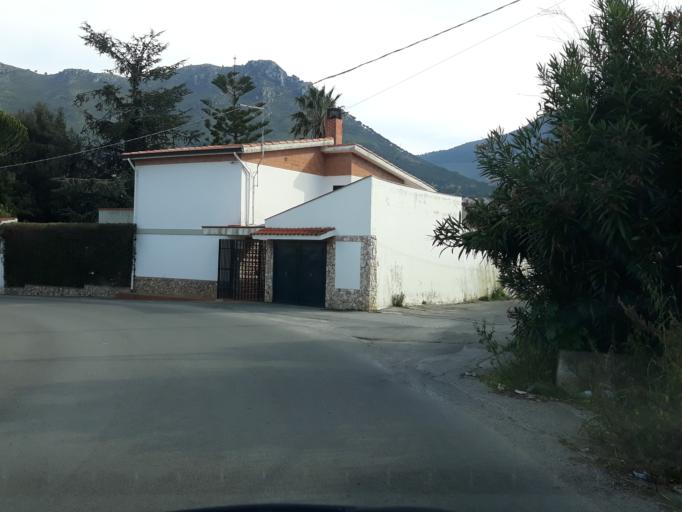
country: IT
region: Sicily
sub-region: Palermo
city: Piano Maglio-Blandino
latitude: 38.0684
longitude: 13.3052
